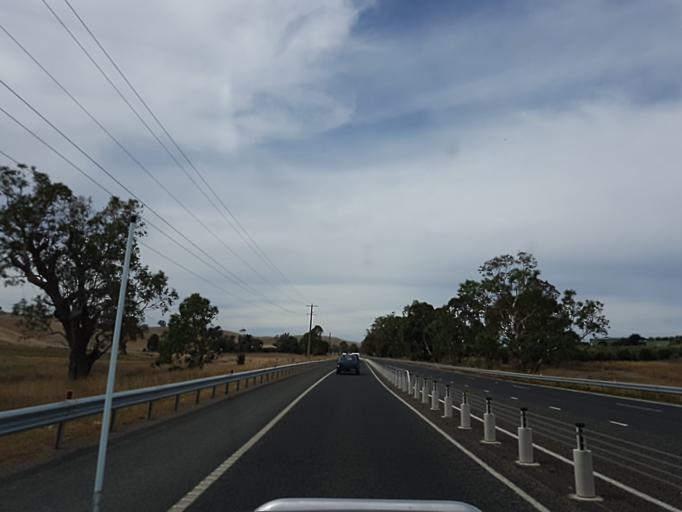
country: AU
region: Victoria
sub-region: Murrindindi
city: Alexandra
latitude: -37.2065
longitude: 145.4591
